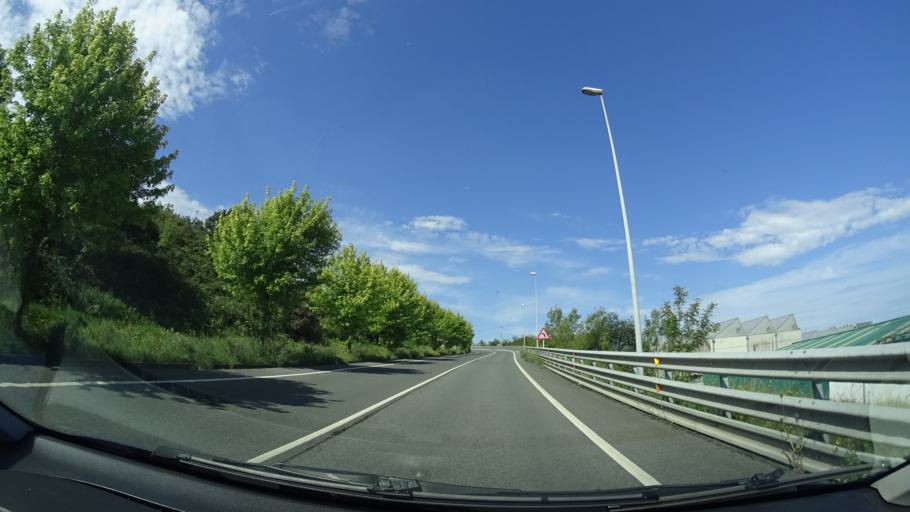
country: ES
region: Basque Country
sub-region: Bizkaia
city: Urtuella
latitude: 43.3058
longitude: -3.0783
